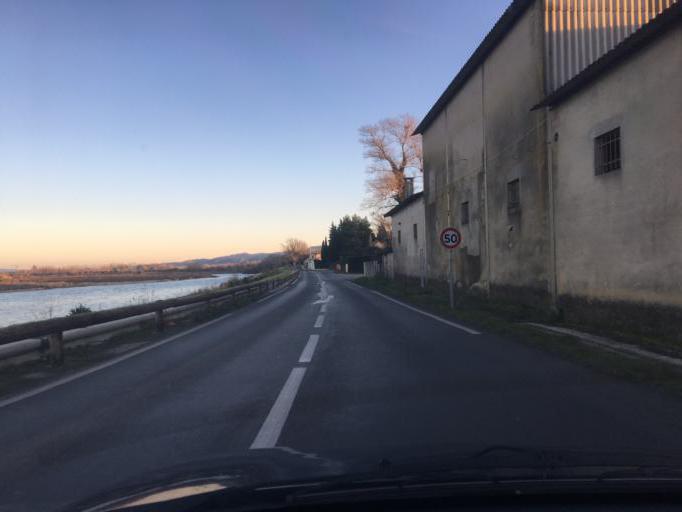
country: FR
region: Provence-Alpes-Cote d'Azur
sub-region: Departement des Bouches-du-Rhone
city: Mallemort
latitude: 43.7366
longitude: 5.1744
